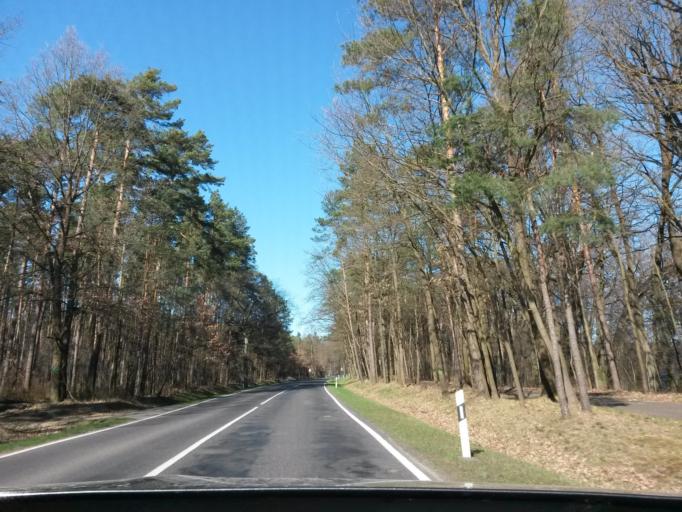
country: DE
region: Brandenburg
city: Grunheide
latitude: 52.4446
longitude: 13.8545
